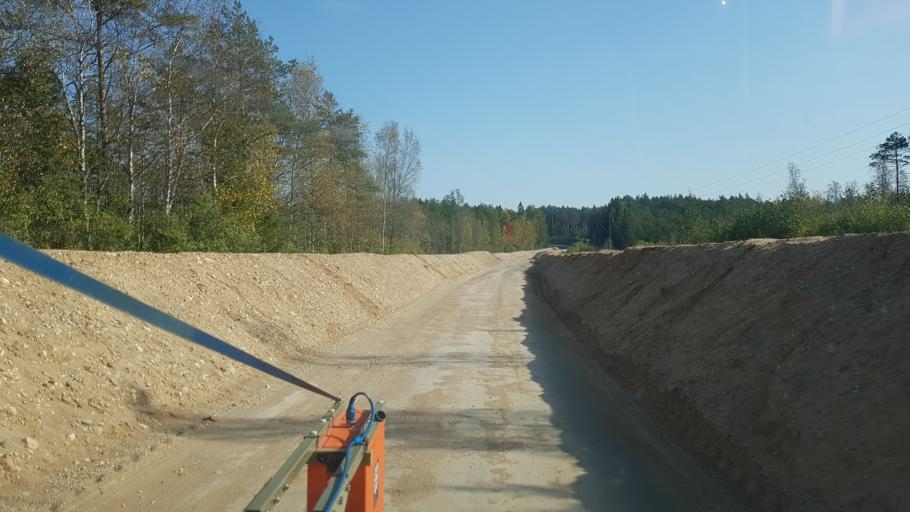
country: EE
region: Valgamaa
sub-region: Torva linn
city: Torva
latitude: 58.0105
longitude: 26.1364
